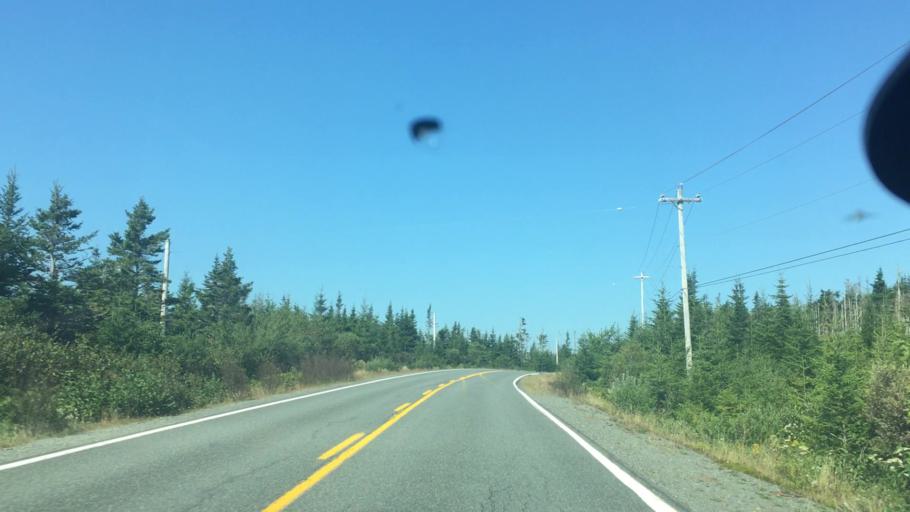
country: CA
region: Nova Scotia
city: Antigonish
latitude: 44.9835
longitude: -62.0952
